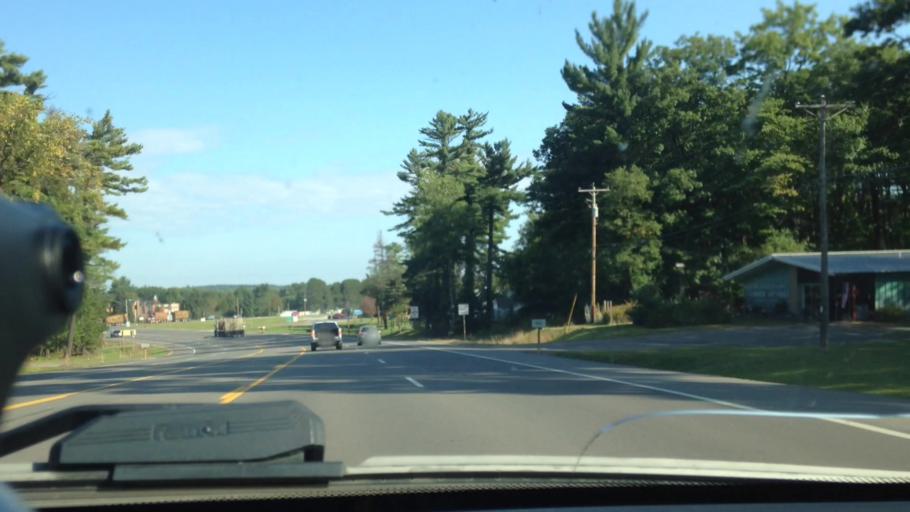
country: US
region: Michigan
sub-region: Dickinson County
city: Iron Mountain
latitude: 45.8603
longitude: -88.0601
